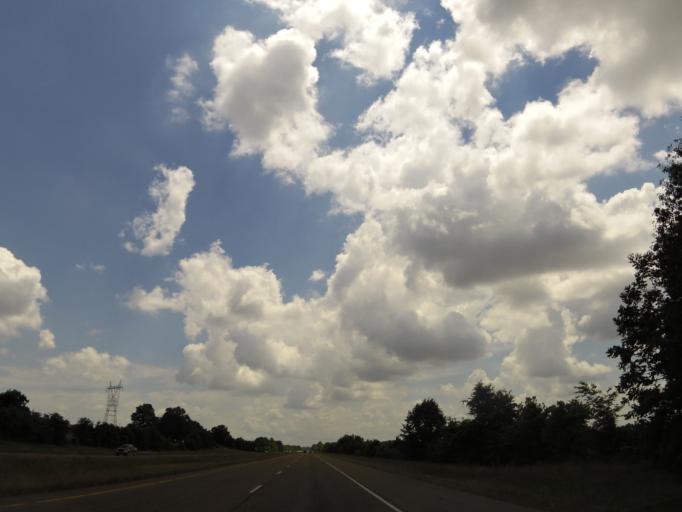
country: US
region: Tennessee
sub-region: Dyer County
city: Dyersburg
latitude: 36.0135
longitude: -89.3413
